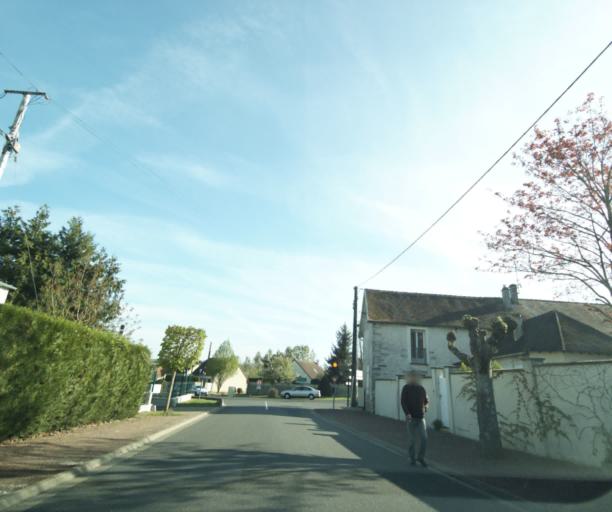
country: FR
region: Ile-de-France
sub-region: Departement de Seine-et-Marne
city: Vernou-la-Celle-sur-Seine
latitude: 48.4629
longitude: 2.8691
